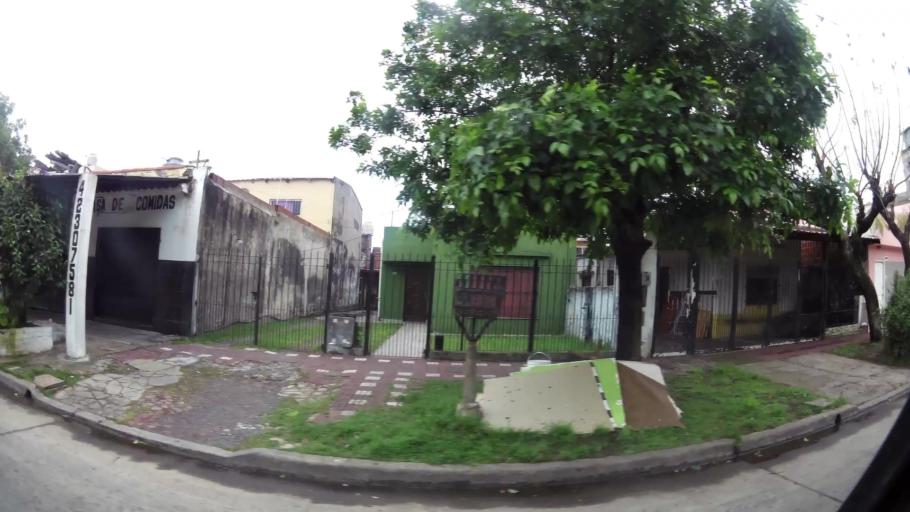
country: AR
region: Buenos Aires
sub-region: Partido de Lanus
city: Lanus
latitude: -34.7264
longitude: -58.3721
